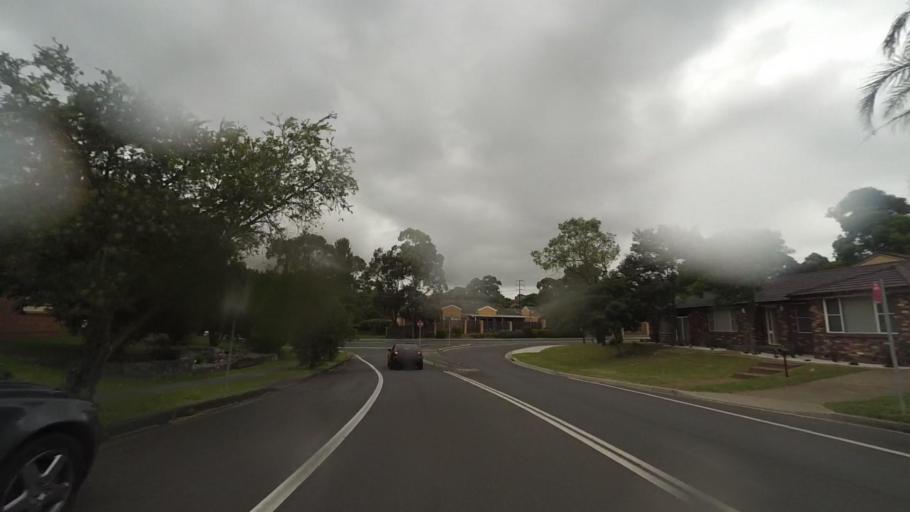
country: AU
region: New South Wales
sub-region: Wollongong
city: Cordeaux Heights
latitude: -34.4437
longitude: 150.8443
